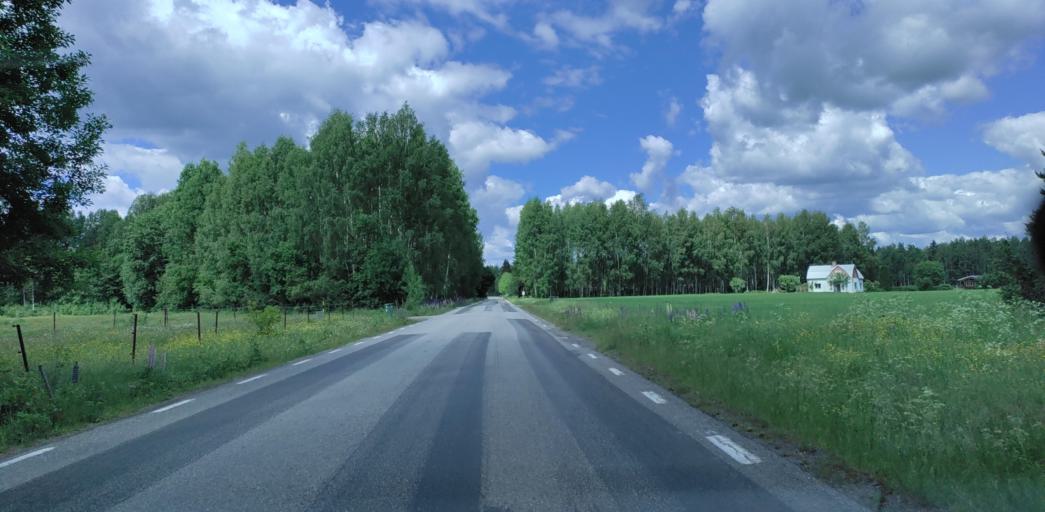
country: SE
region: Vaermland
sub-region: Hagfors Kommun
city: Ekshaerad
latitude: 60.0678
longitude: 13.5401
